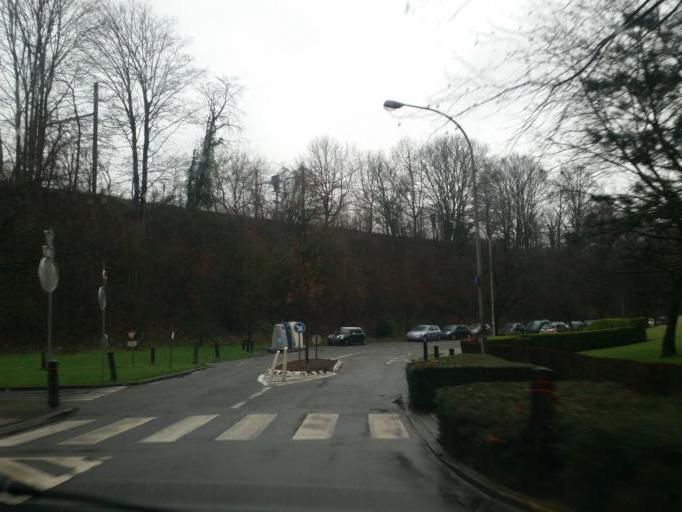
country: BE
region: Brussels Capital
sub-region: Bruxelles-Capitale
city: Brussels
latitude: 50.8120
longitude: 4.4011
